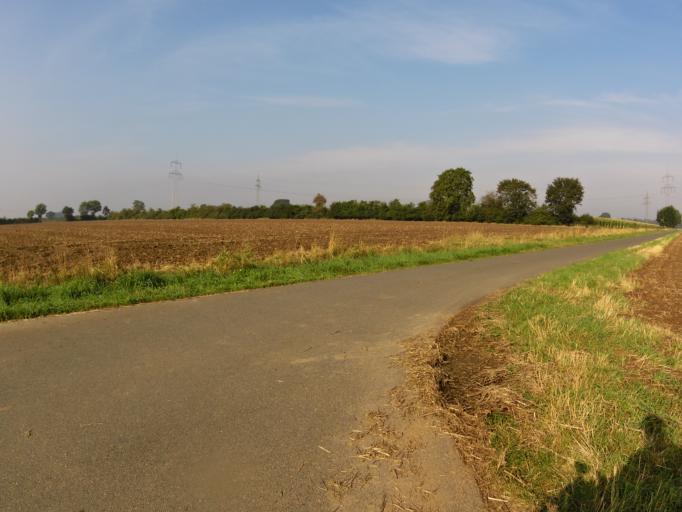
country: DE
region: Lower Saxony
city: Verden
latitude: 52.9491
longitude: 9.2102
